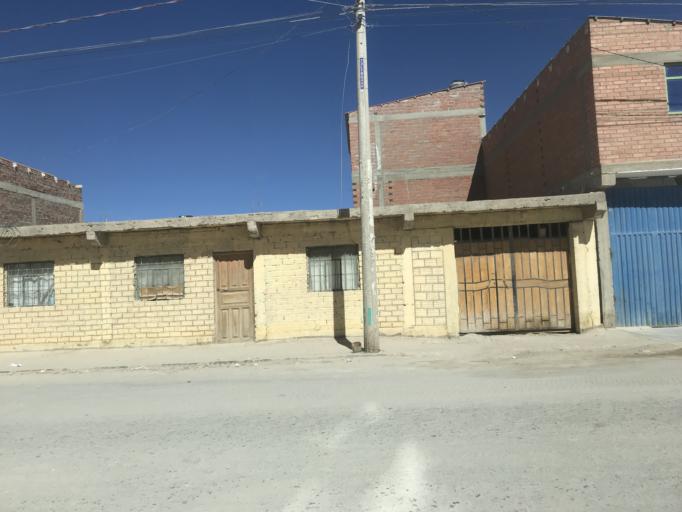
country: BO
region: Potosi
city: Uyuni
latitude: -20.4551
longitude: -66.8296
